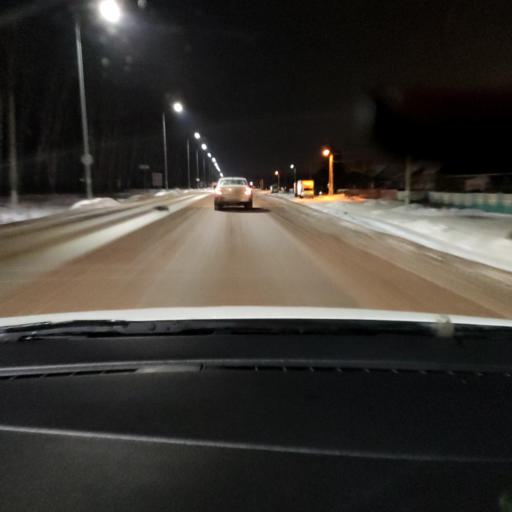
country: RU
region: Tatarstan
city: Stolbishchi
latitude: 55.6273
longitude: 49.1391
